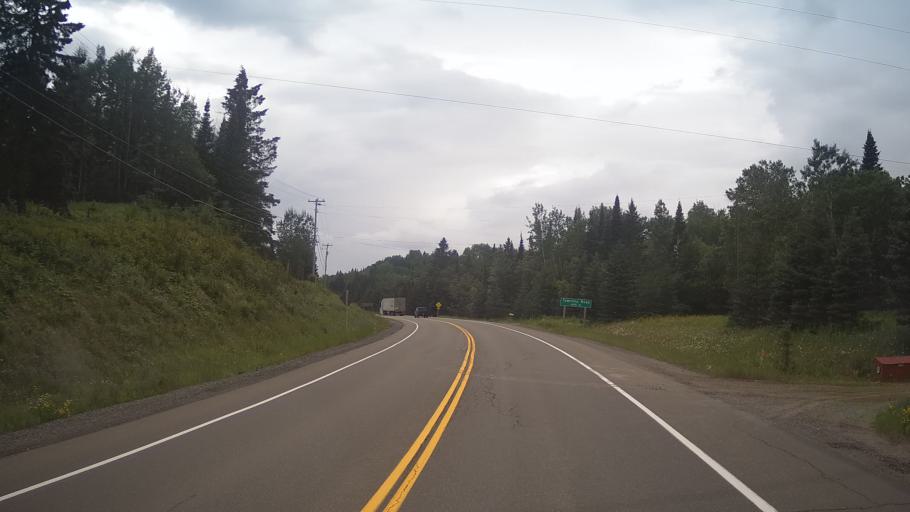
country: CA
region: Ontario
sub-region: Thunder Bay District
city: Thunder Bay
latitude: 48.4974
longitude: -89.4217
